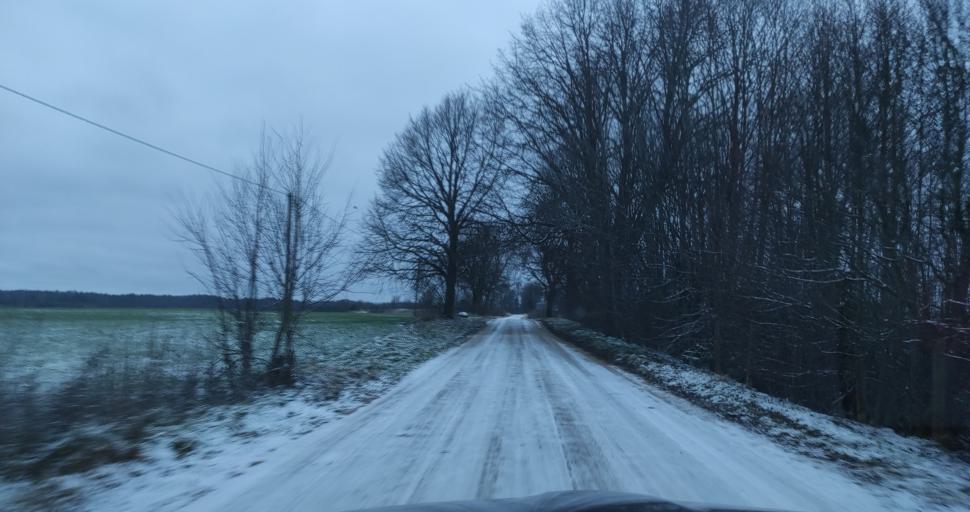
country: LV
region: Kuldigas Rajons
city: Kuldiga
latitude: 56.9694
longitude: 22.0625
